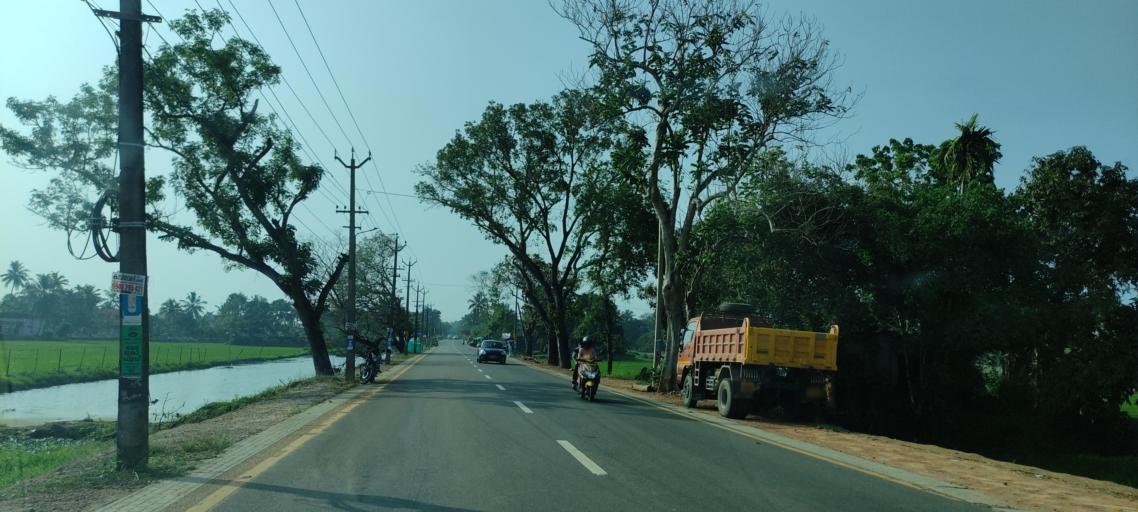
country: IN
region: Kerala
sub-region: Kottayam
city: Changanacheri
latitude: 9.3674
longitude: 76.4332
